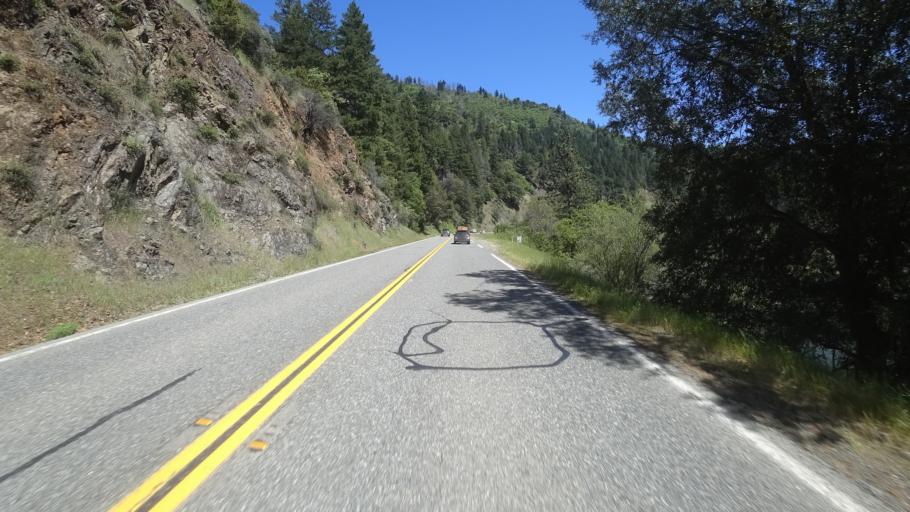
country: US
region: California
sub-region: Trinity County
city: Hayfork
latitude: 40.7846
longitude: -123.3413
